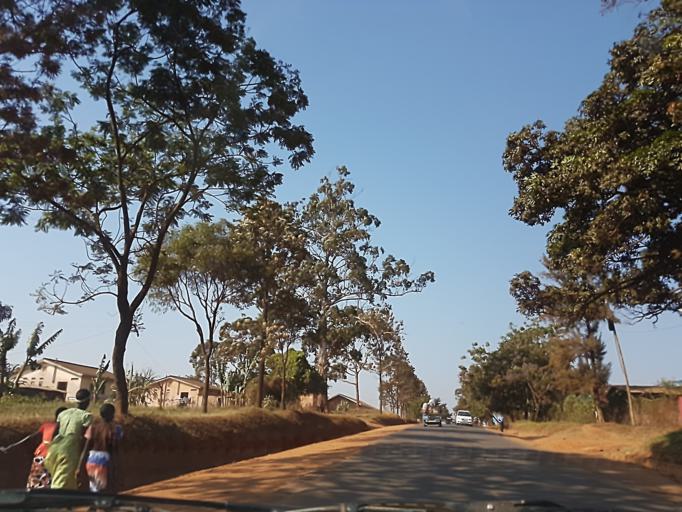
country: UG
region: Central Region
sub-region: Wakiso District
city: Kireka
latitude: 0.3378
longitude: 32.6149
